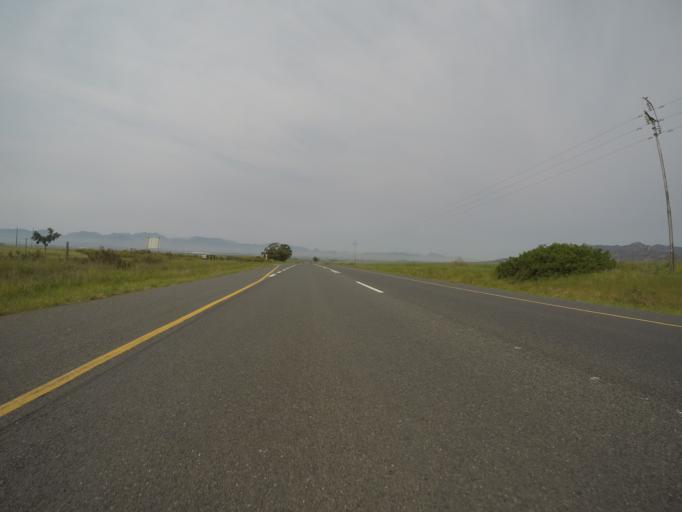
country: ZA
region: Western Cape
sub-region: West Coast District Municipality
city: Malmesbury
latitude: -33.5299
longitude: 18.8500
